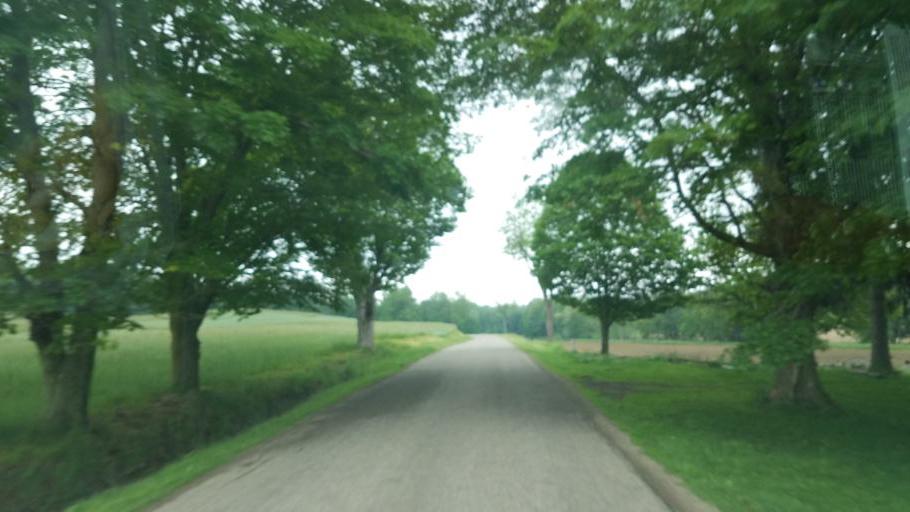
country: US
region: Ohio
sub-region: Richland County
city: Lincoln Heights
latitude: 40.7460
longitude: -82.4302
